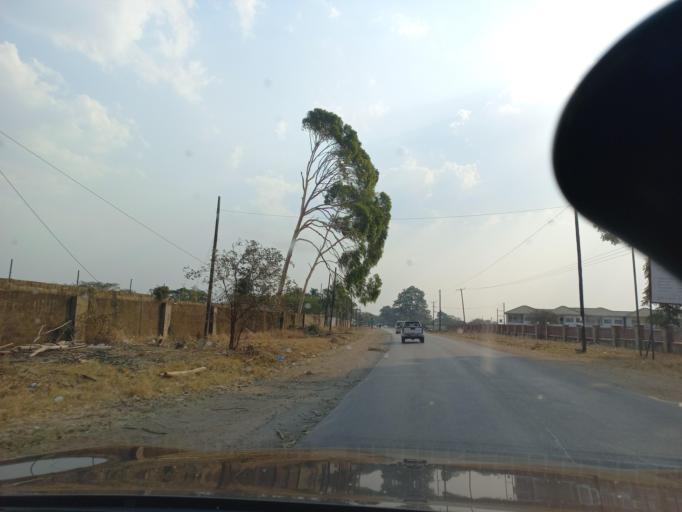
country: ZM
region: Lusaka
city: Lusaka
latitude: -15.4673
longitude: 28.2266
